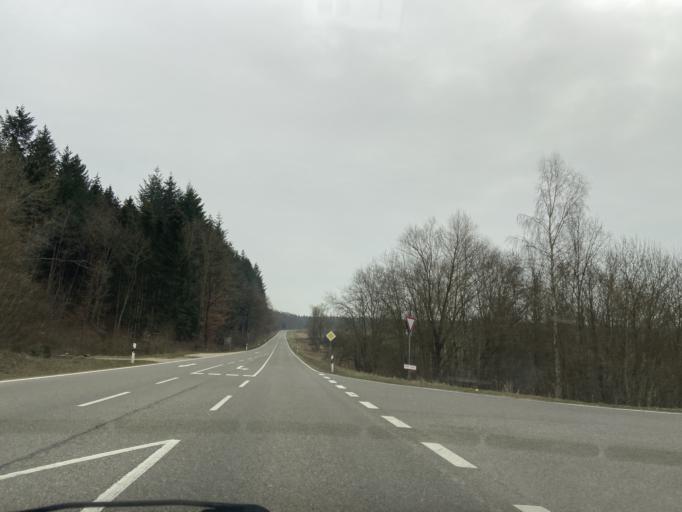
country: DE
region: Baden-Wuerttemberg
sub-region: Tuebingen Region
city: Krauchenwies
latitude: 48.0153
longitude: 9.2625
